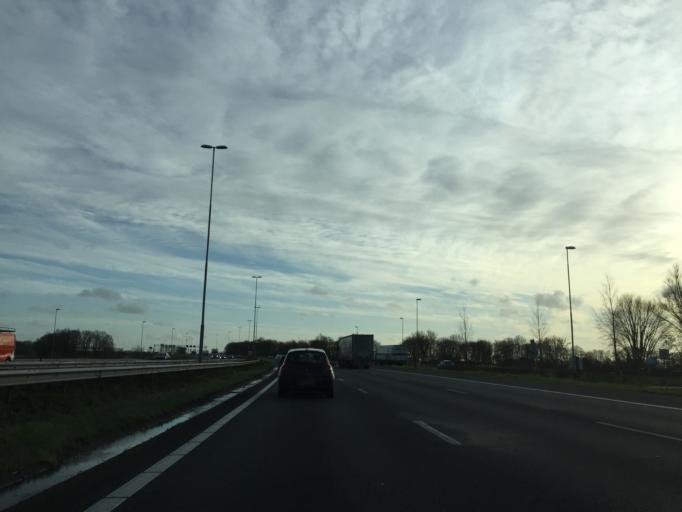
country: NL
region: Gelderland
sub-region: Gemeente Maasdriel
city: Hedel
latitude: 51.7750
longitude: 5.2594
